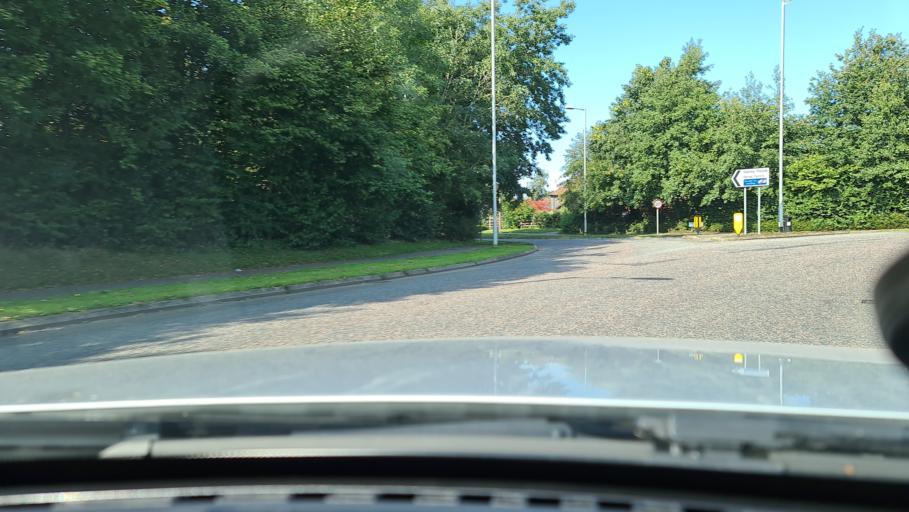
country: GB
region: England
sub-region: Northamptonshire
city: Daventry
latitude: 52.2733
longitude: -1.1581
